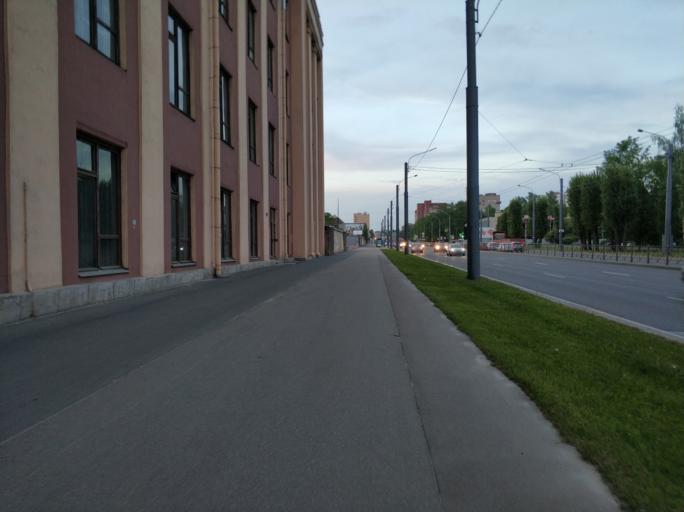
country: RU
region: Leningrad
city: Svetlanovskiy
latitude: 60.0071
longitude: 30.3372
